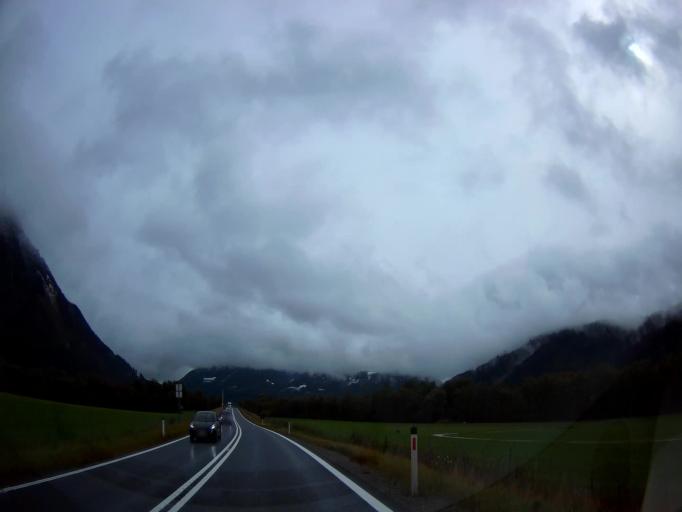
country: AT
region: Styria
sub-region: Politischer Bezirk Liezen
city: Liezen
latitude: 47.5561
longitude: 14.2653
